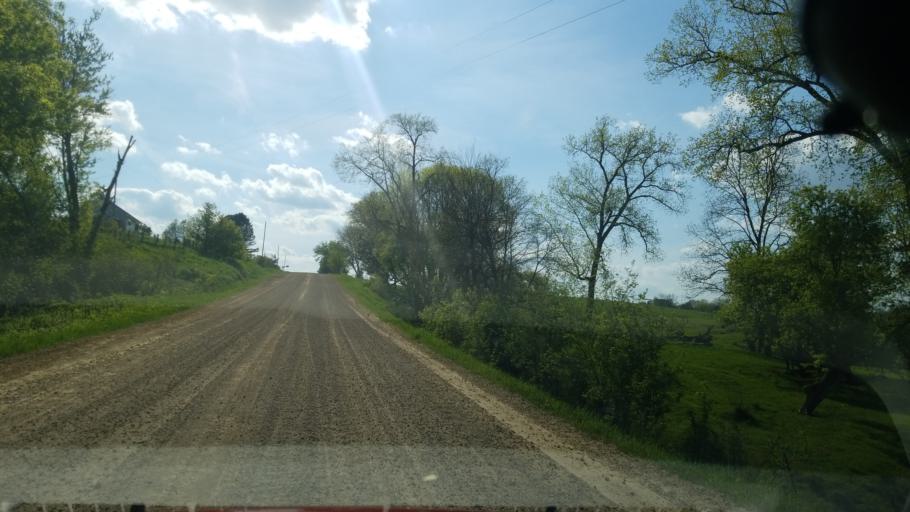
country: US
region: Iowa
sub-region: Jackson County
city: Maquoketa
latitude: 42.2150
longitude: -90.6973
